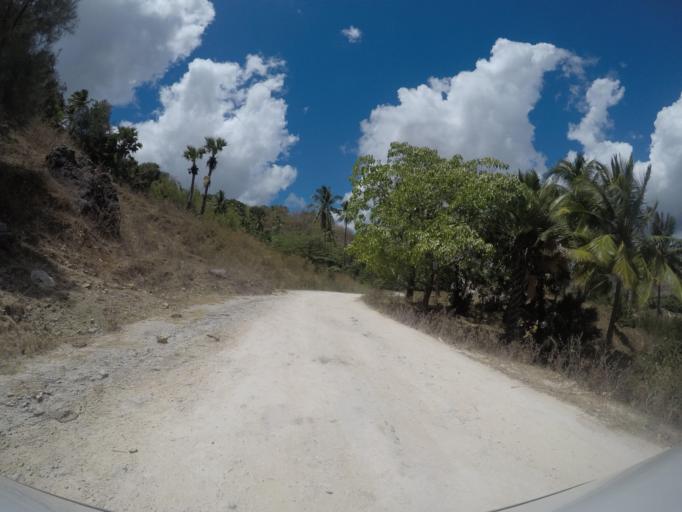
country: TL
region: Baucau
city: Baucau
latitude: -8.4869
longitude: 126.6440
